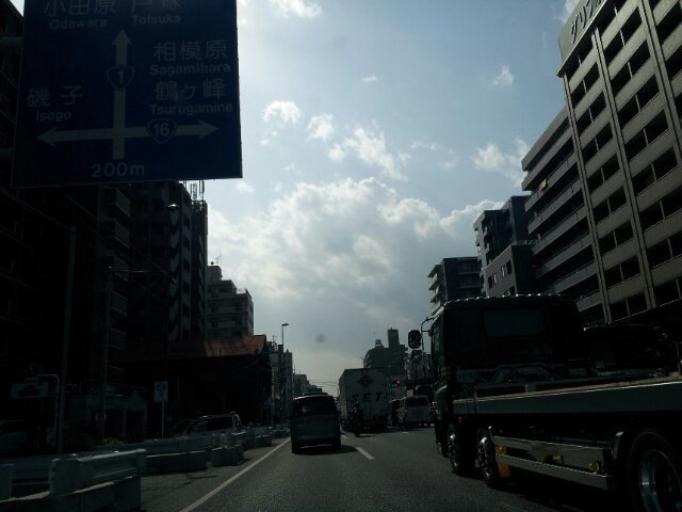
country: JP
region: Kanagawa
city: Yokohama
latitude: 35.4559
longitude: 139.6163
